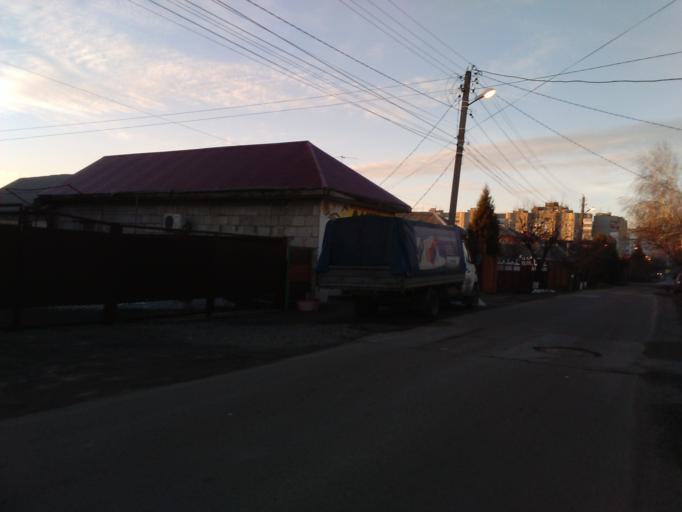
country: RU
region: Rostov
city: Bataysk
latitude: 47.1515
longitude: 39.7408
